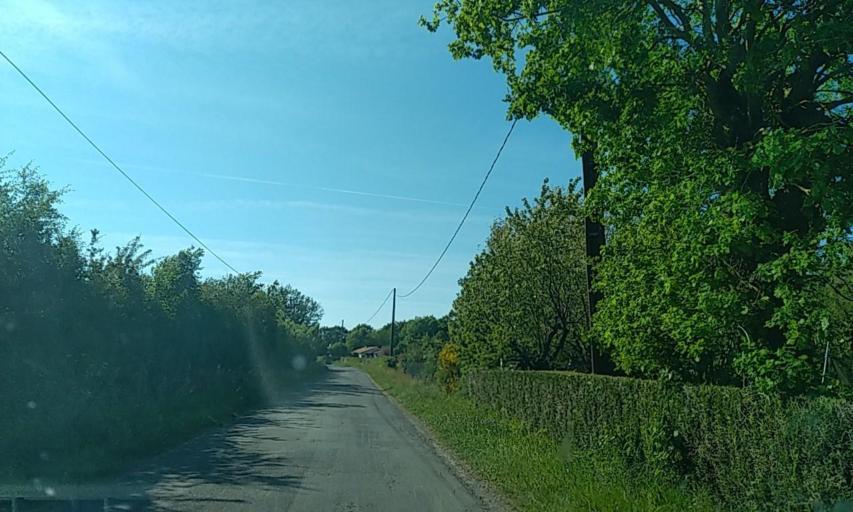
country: FR
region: Poitou-Charentes
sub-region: Departement des Deux-Sevres
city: Boisme
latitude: 46.7991
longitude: -0.4381
